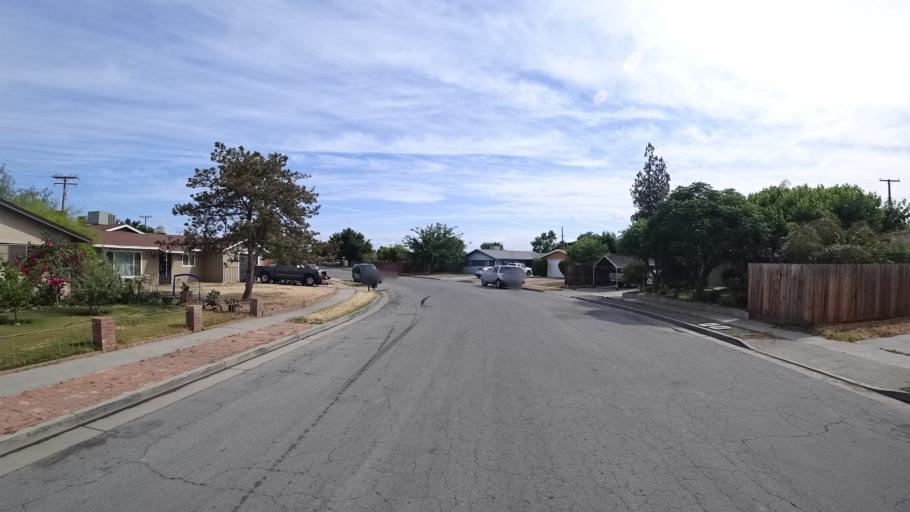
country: US
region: California
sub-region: Kings County
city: Hanford
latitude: 36.3168
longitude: -119.6683
